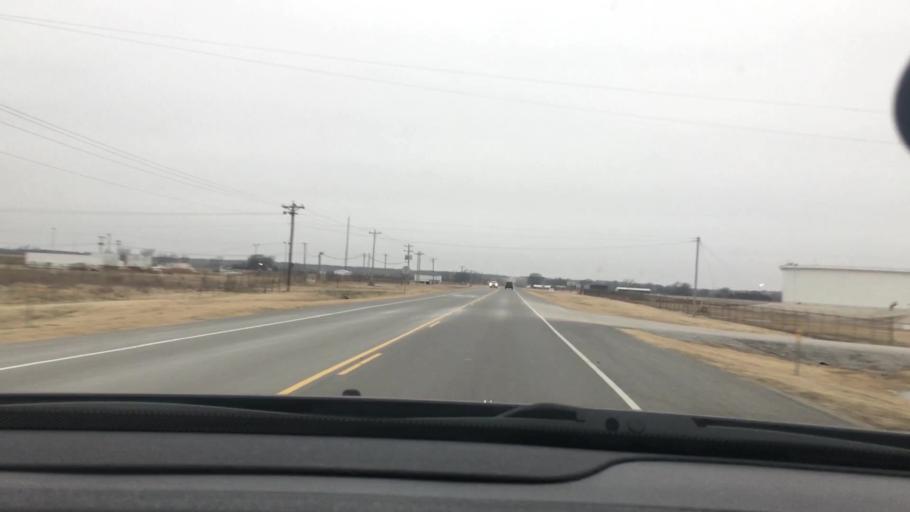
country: US
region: Oklahoma
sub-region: Garvin County
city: Wynnewood
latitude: 34.6227
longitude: -97.1699
